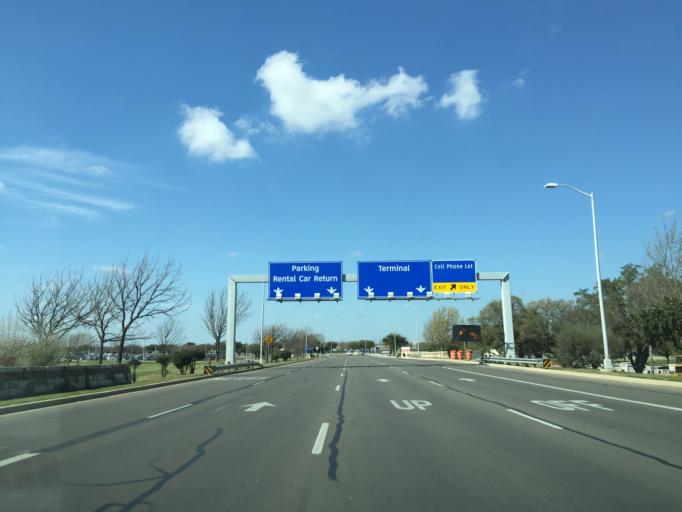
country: US
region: Texas
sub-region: Travis County
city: Hornsby Bend
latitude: 30.2100
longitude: -97.6649
